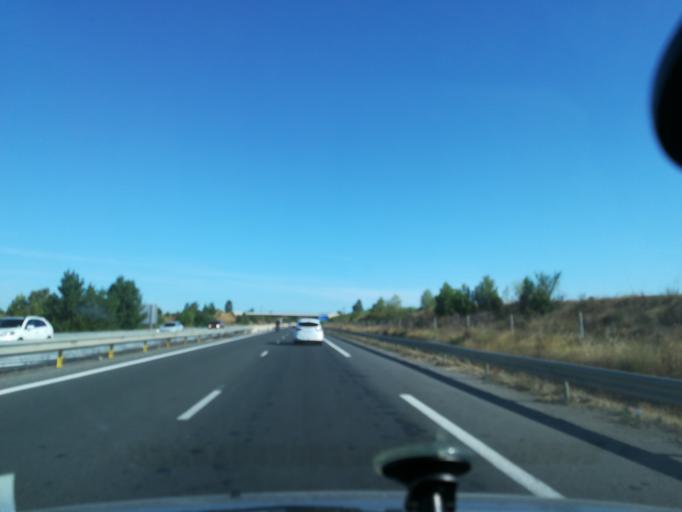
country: FR
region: Languedoc-Roussillon
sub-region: Departement de l'Herault
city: Villeneuve-les-Beziers
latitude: 43.3373
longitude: 3.2811
